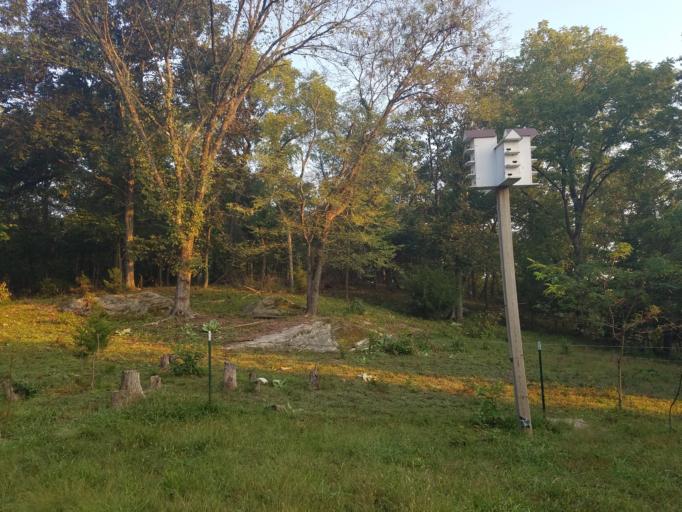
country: US
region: Missouri
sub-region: Moniteau County
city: California
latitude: 38.7447
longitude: -92.6285
